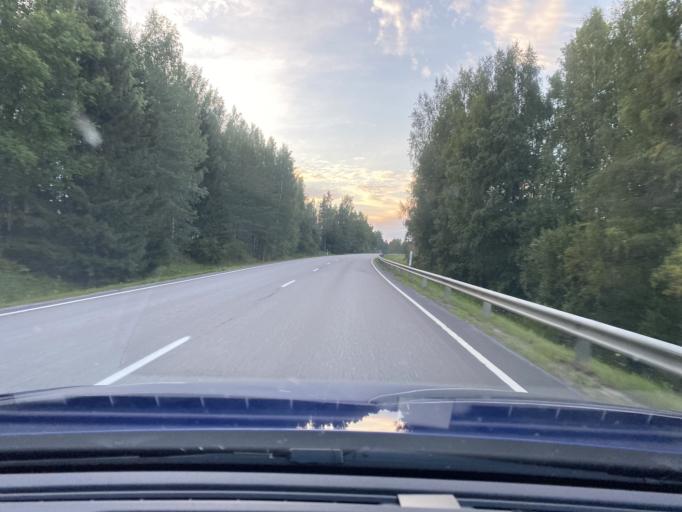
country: FI
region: Satakunta
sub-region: Pohjois-Satakunta
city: Honkajoki
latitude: 61.8835
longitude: 22.2920
